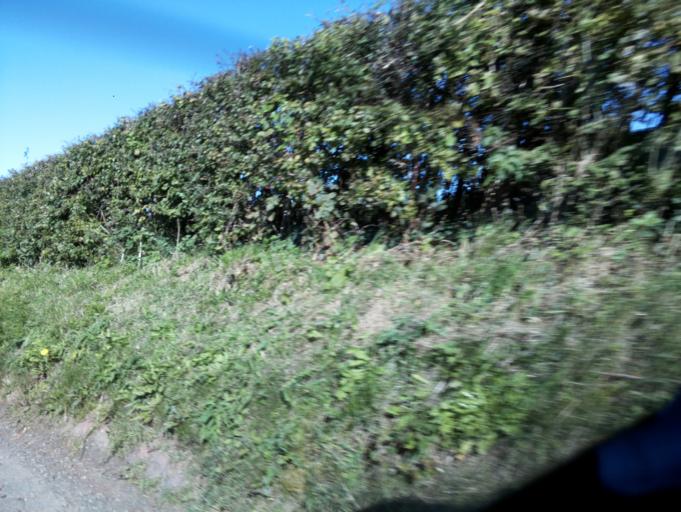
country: GB
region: Wales
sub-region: Torfaen County Borough
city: Cwmbran
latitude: 51.6148
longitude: -3.0500
